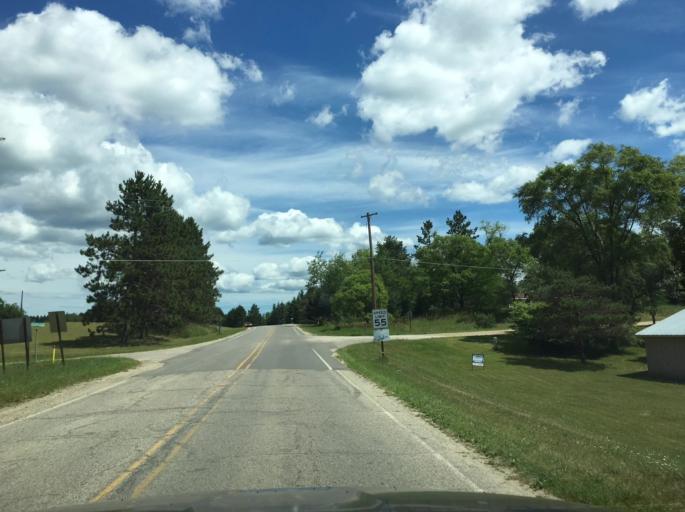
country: US
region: Michigan
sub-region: Osceola County
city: Reed City
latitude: 43.8577
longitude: -85.4437
